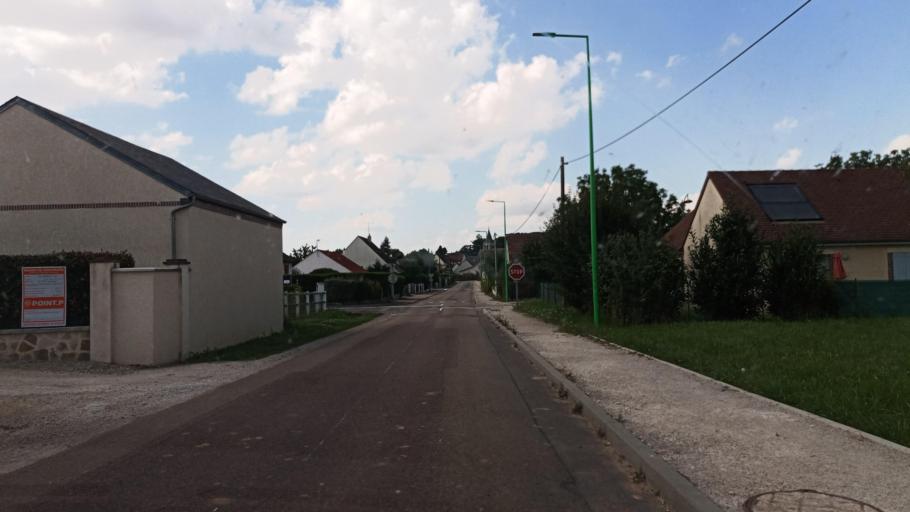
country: FR
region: Bourgogne
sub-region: Departement de l'Yonne
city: Saint-Valerien
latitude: 48.1754
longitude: 3.0974
